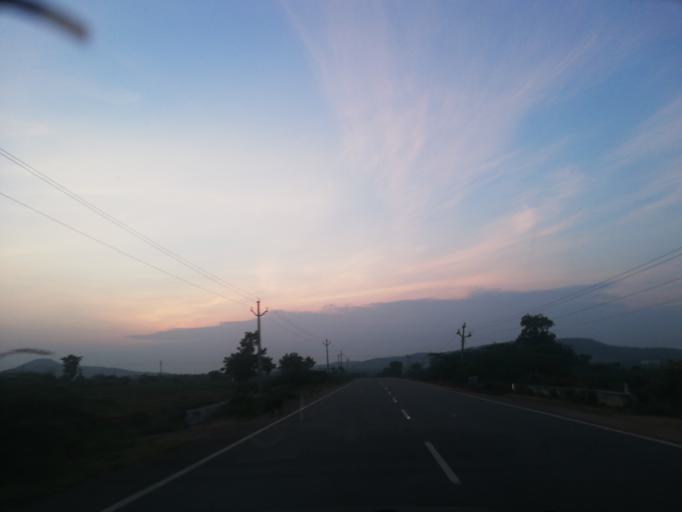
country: IN
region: Andhra Pradesh
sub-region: Guntur
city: Macherla
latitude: 16.6739
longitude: 79.2723
